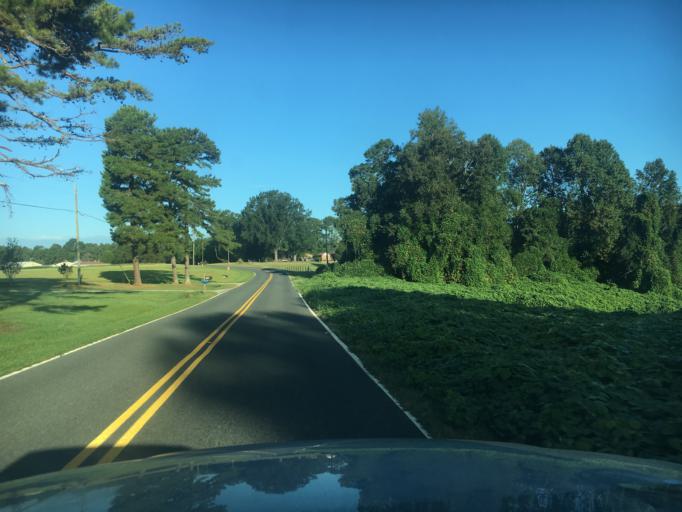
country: US
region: South Carolina
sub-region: Spartanburg County
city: Woodruff
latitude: 34.6378
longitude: -82.0149
